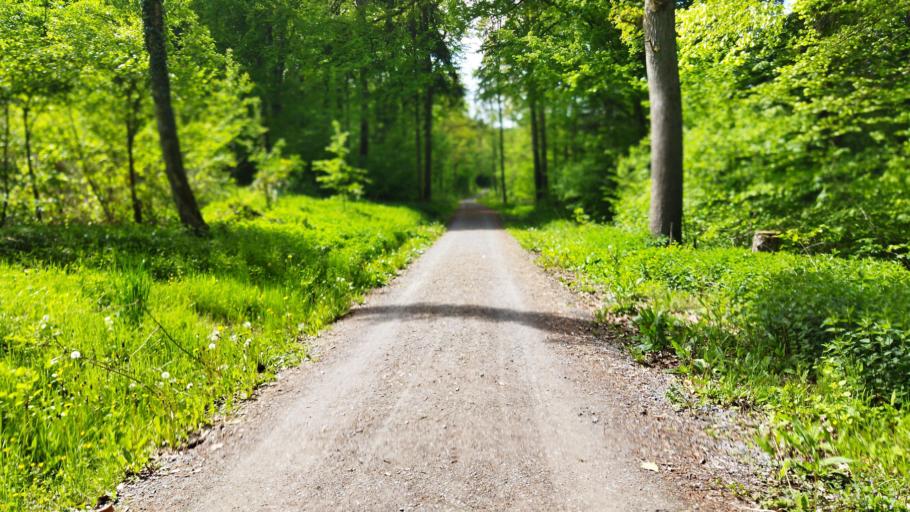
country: DE
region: Baden-Wuerttemberg
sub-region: Regierungsbezirk Stuttgart
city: Bad Rappenau
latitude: 49.2048
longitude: 9.1239
